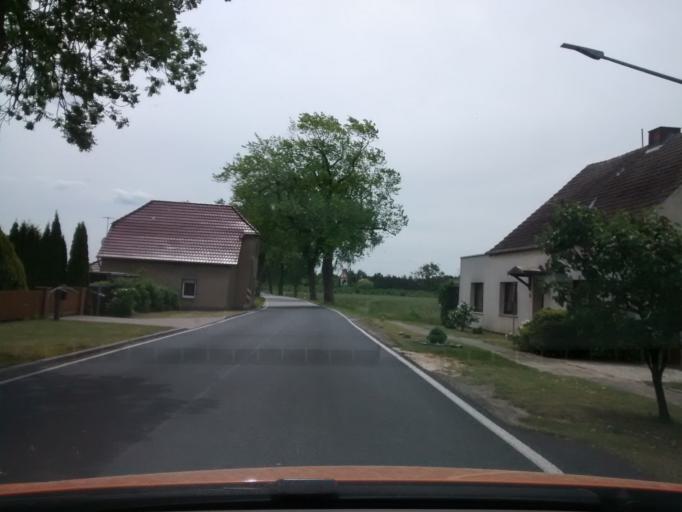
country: DE
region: Brandenburg
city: Juterbog
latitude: 51.8989
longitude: 13.1404
